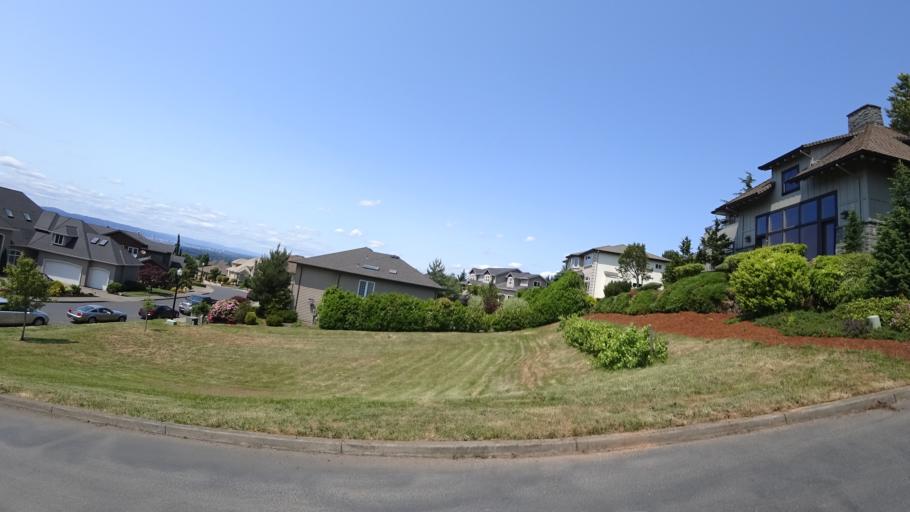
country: US
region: Oregon
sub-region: Multnomah County
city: Lents
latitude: 45.4542
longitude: -122.5574
